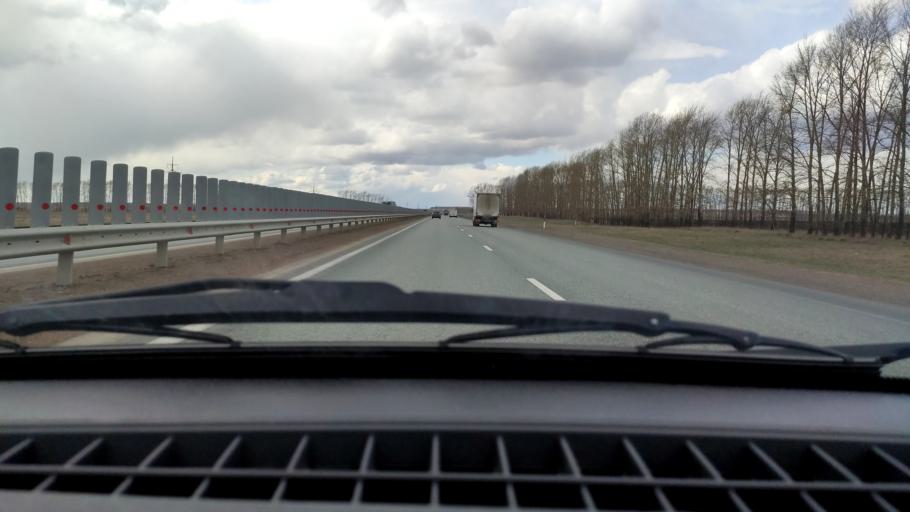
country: RU
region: Bashkortostan
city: Asanovo
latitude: 54.9918
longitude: 55.5123
